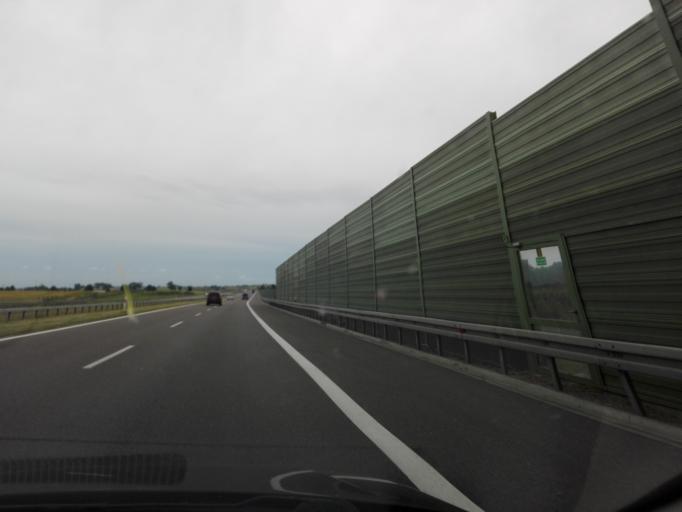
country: PL
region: Lublin Voivodeship
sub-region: Powiat lubelski
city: Garbow
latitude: 51.3605
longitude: 22.3595
